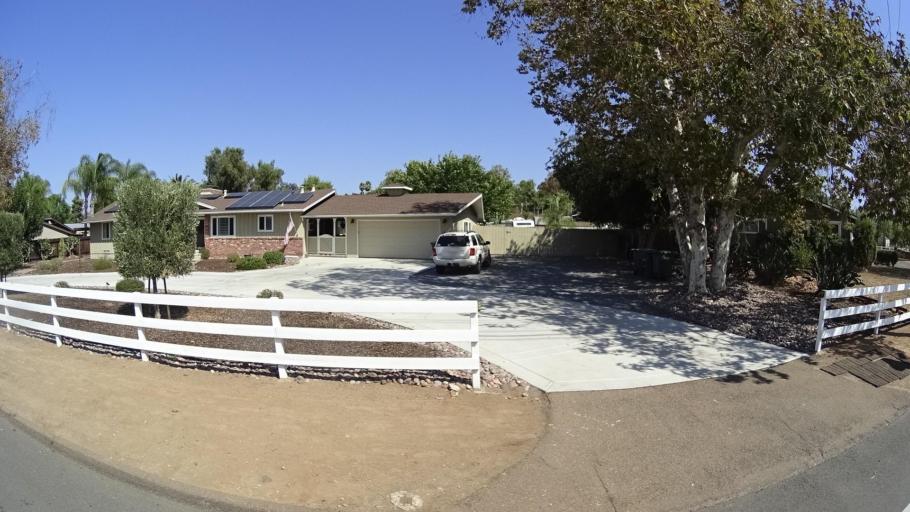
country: US
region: California
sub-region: San Diego County
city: Granite Hills
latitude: 32.7934
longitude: -116.9210
